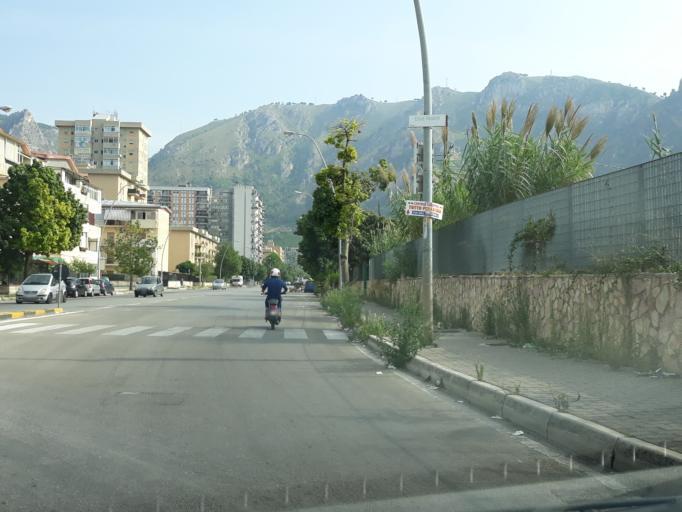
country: IT
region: Sicily
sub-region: Palermo
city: Villa Ciambra
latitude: 38.0847
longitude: 13.3557
